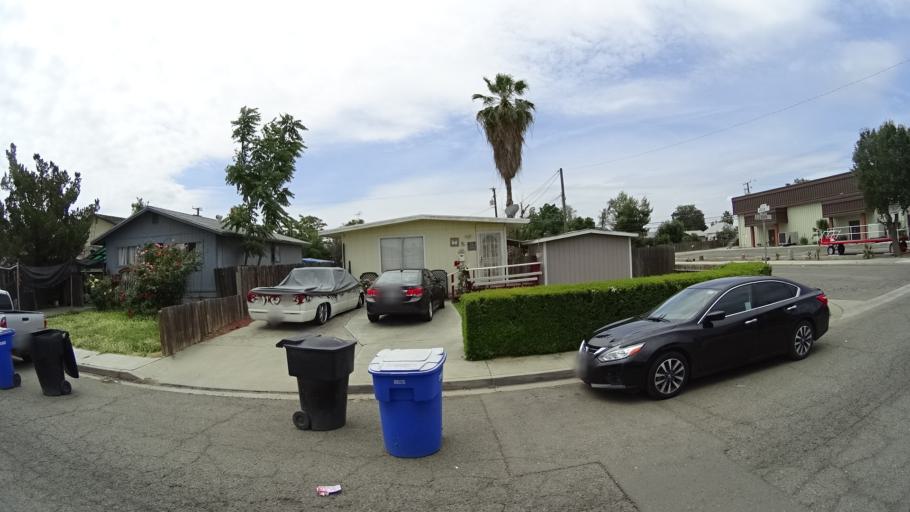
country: US
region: California
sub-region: Kings County
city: Hanford
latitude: 36.3312
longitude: -119.6410
